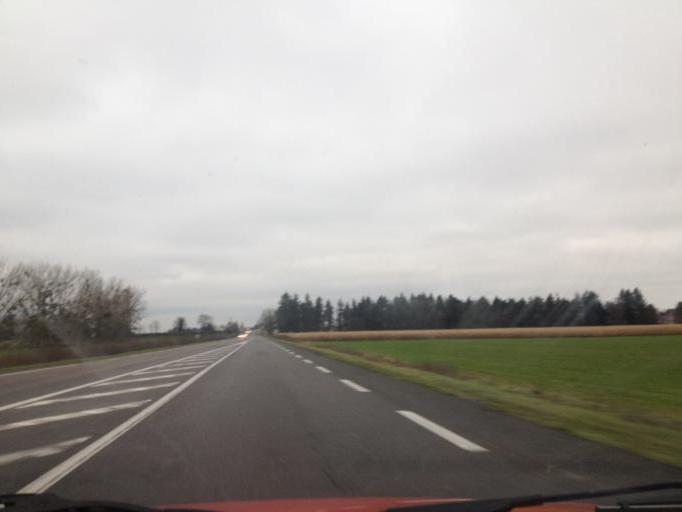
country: FR
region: Auvergne
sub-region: Departement de l'Allier
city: Bessay-sur-Allier
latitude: 46.4652
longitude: 3.3686
